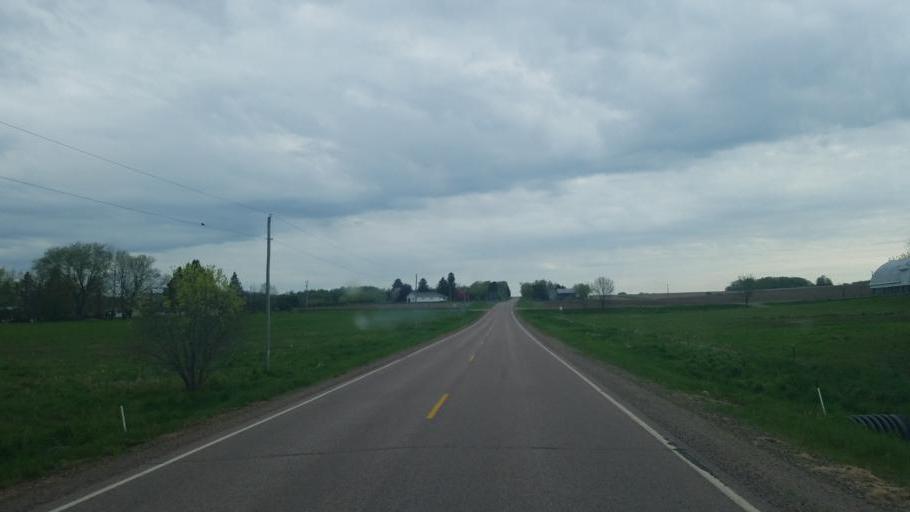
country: US
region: Wisconsin
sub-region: Wood County
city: Marshfield
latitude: 44.5826
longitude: -90.2994
